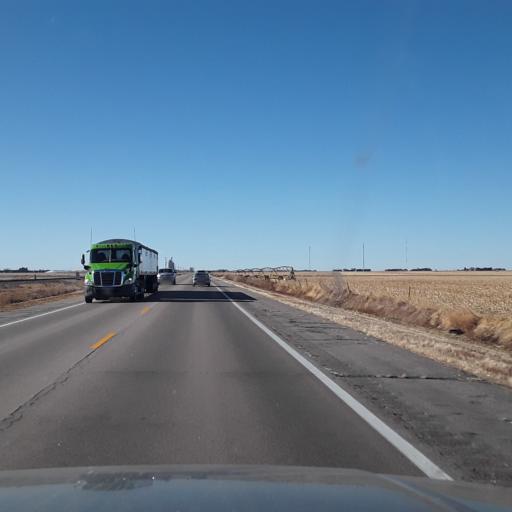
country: US
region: Nebraska
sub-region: Kearney County
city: Minden
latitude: 40.4900
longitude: -99.0422
